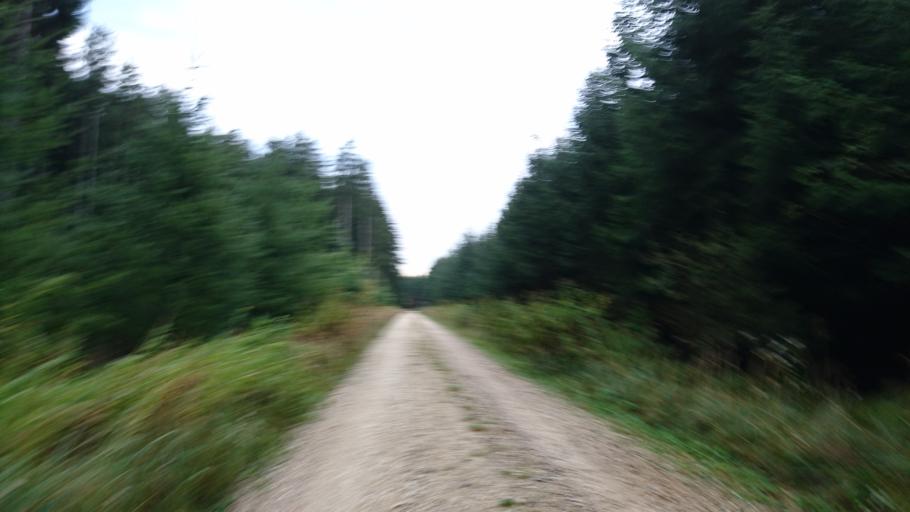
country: DE
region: Bavaria
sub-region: Swabia
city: Welden
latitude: 48.4379
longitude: 10.6261
